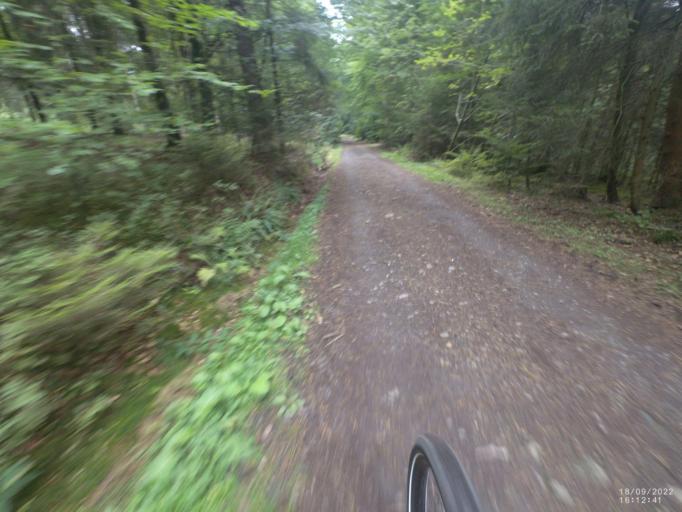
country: DE
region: Rheinland-Pfalz
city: Deudesfeld
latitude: 50.1091
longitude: 6.7236
